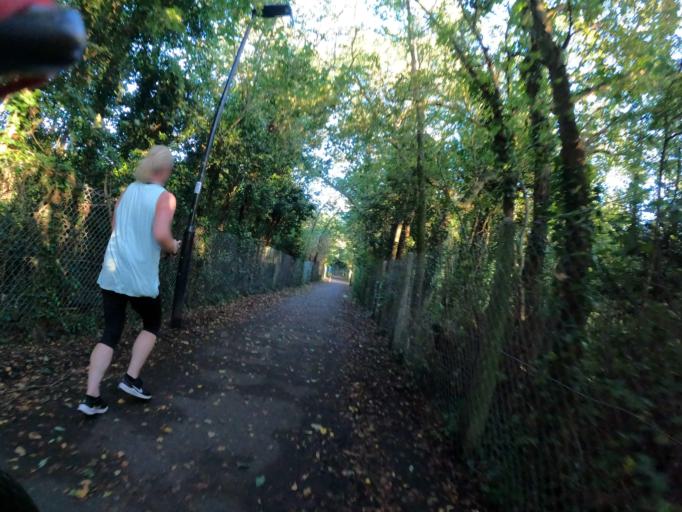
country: GB
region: England
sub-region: Greater London
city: Ealing Broadway
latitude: 51.5297
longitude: -0.3209
